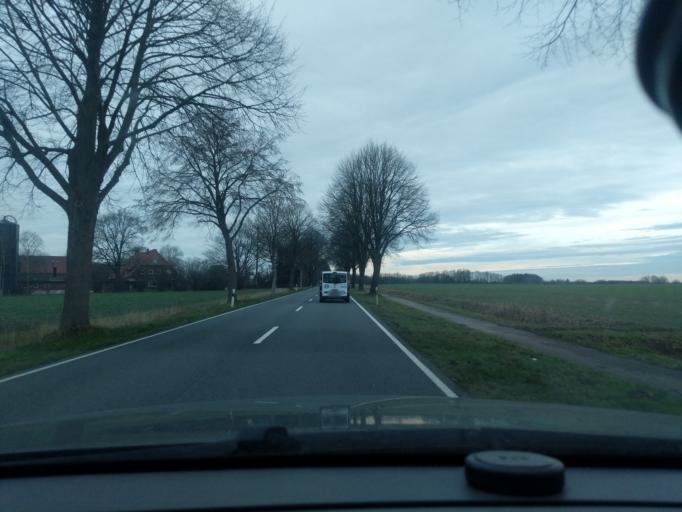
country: DE
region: Lower Saxony
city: Beckdorf
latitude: 53.4019
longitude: 9.6102
